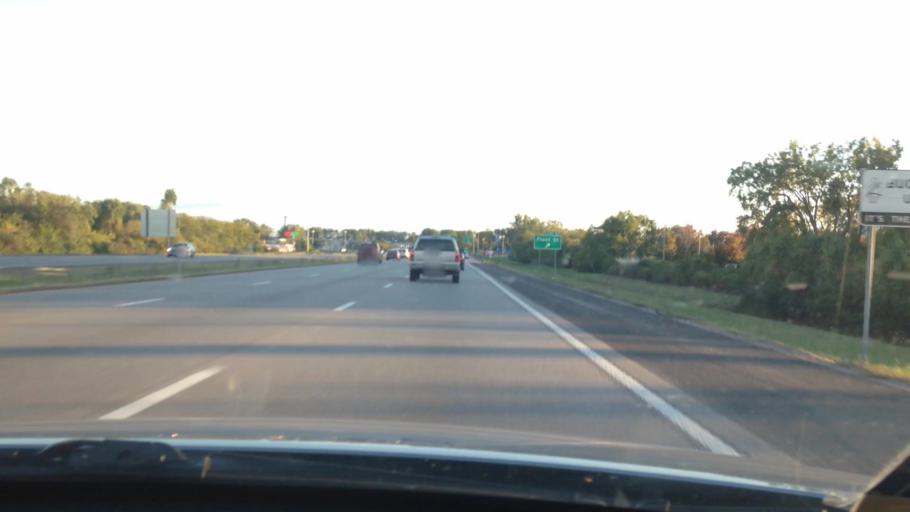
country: US
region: Missouri
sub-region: Jackson County
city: Sugar Creek
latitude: 39.1375
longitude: -94.4990
